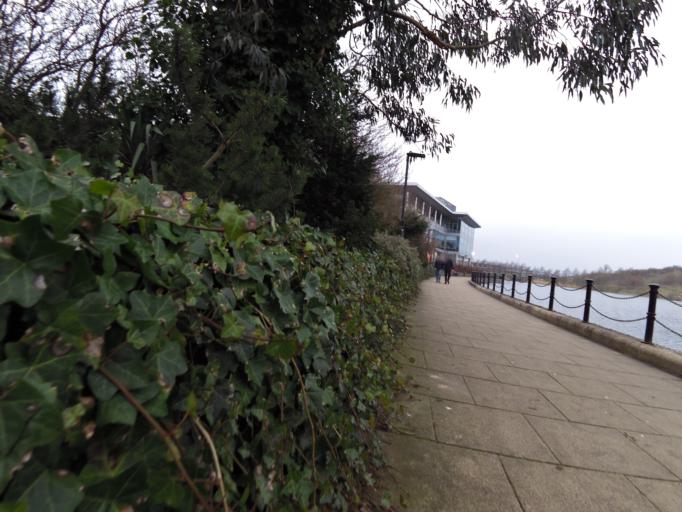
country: GB
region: England
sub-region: Doncaster
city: Doncaster
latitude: 53.5068
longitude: -1.1080
